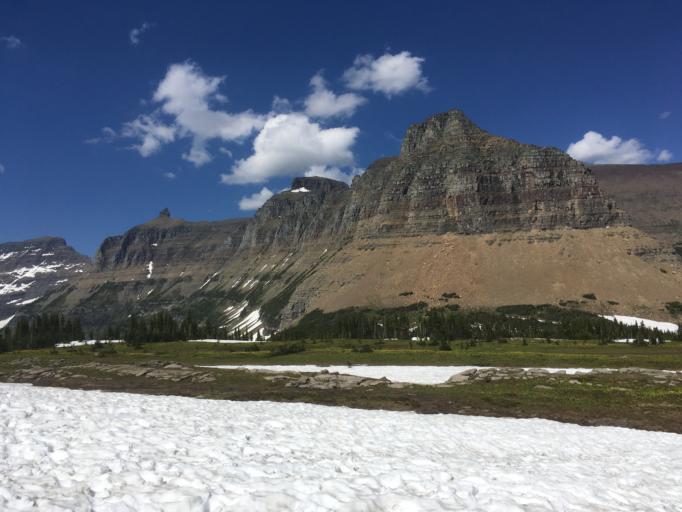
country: US
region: Montana
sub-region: Flathead County
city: Columbia Falls
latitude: 48.6949
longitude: -113.7218
